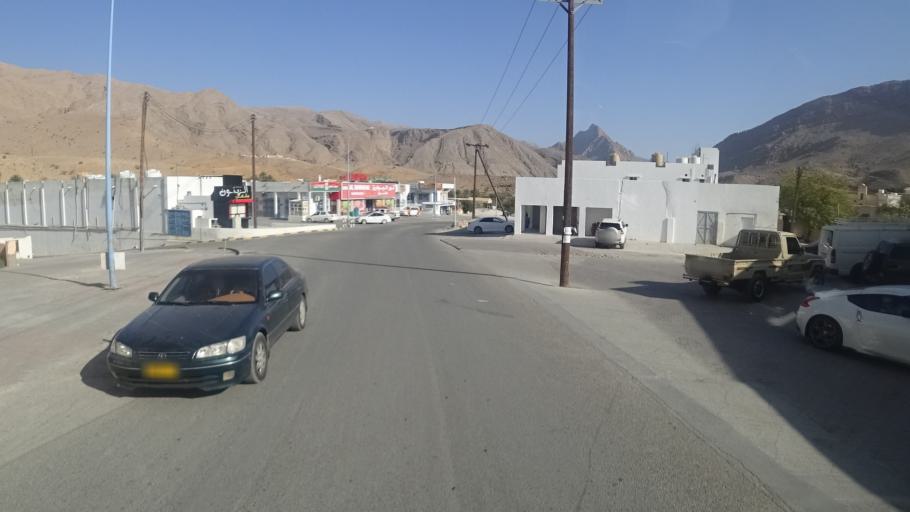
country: OM
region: Ash Sharqiyah
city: Badiyah
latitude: 22.5775
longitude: 59.0968
